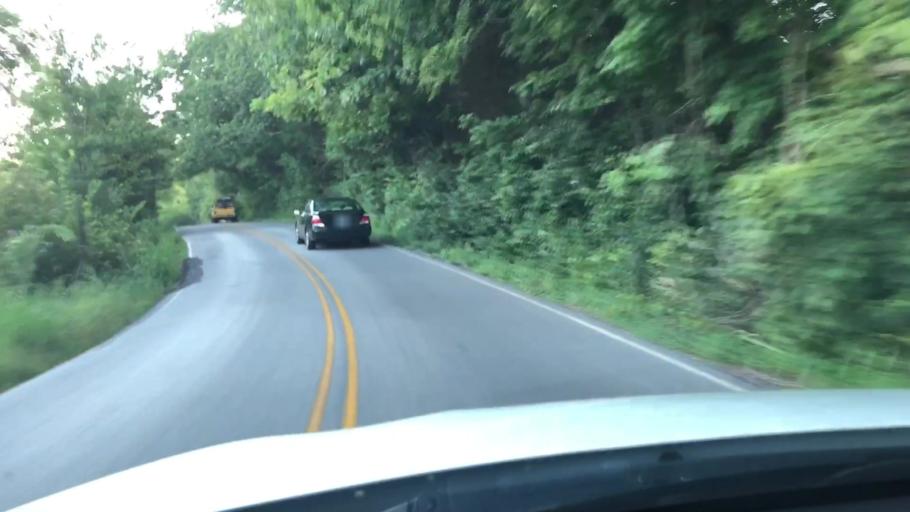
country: US
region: Kentucky
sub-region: Jefferson County
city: Middletown
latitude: 38.2032
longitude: -85.4892
